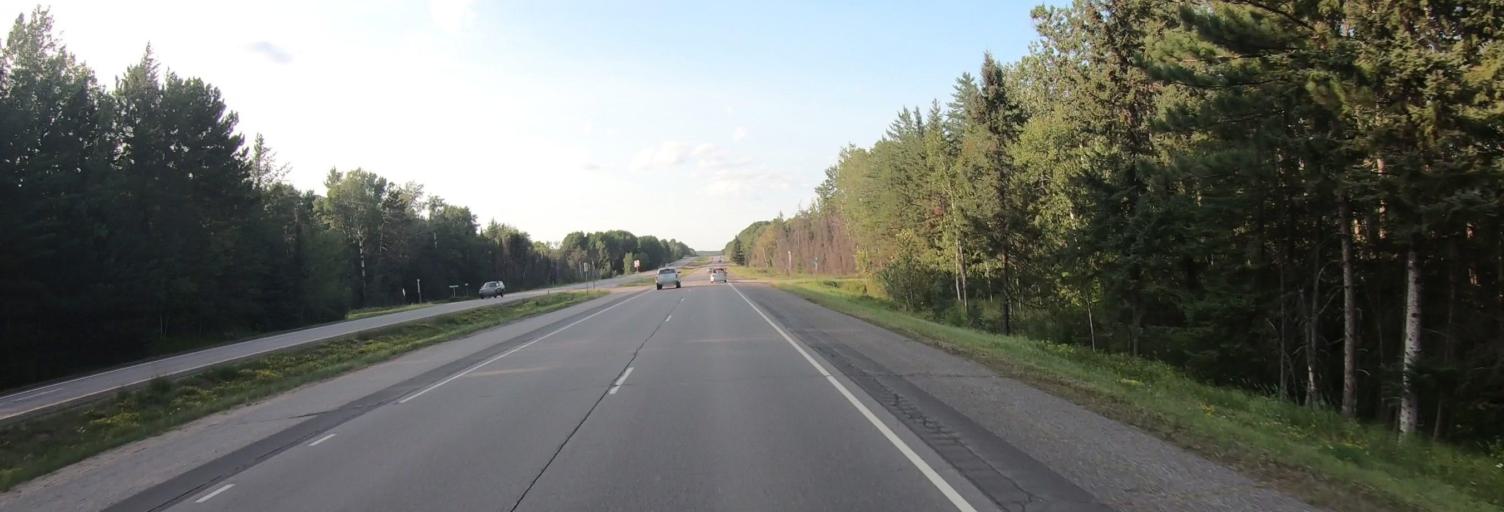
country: US
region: Minnesota
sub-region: Saint Louis County
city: Eveleth
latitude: 47.4082
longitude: -92.5201
